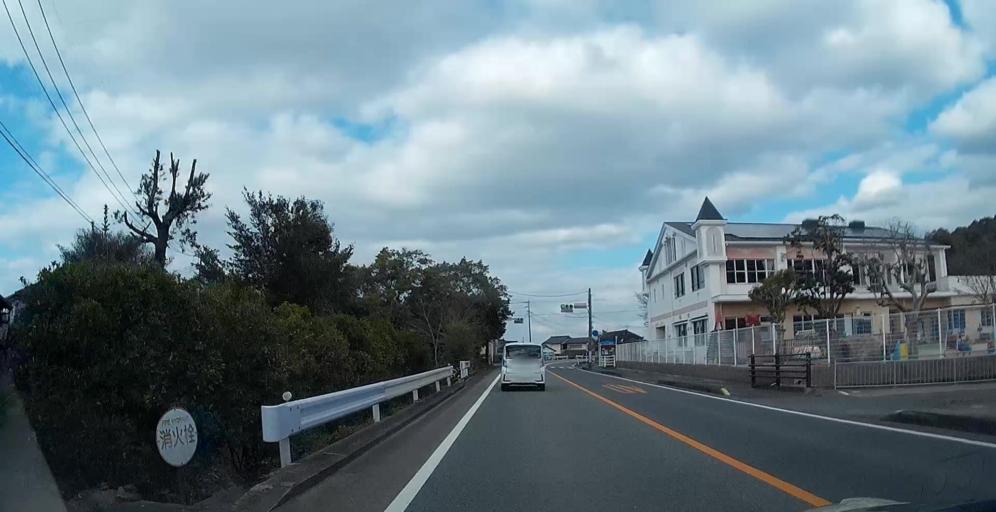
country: JP
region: Kumamoto
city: Yatsushiro
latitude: 32.4456
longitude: 130.5867
